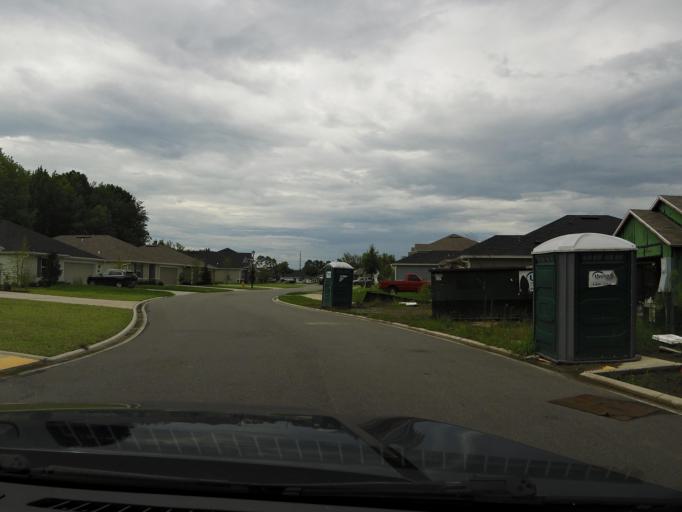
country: US
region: Florida
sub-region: Nassau County
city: Nassau Village-Ratliff
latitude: 30.4482
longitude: -81.7540
